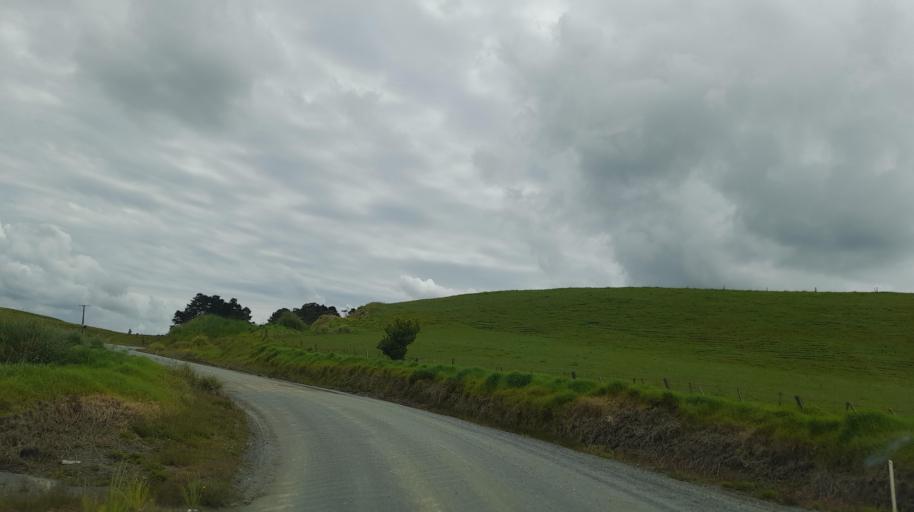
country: NZ
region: Auckland
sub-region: Auckland
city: Wellsford
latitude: -36.2425
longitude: 174.4240
